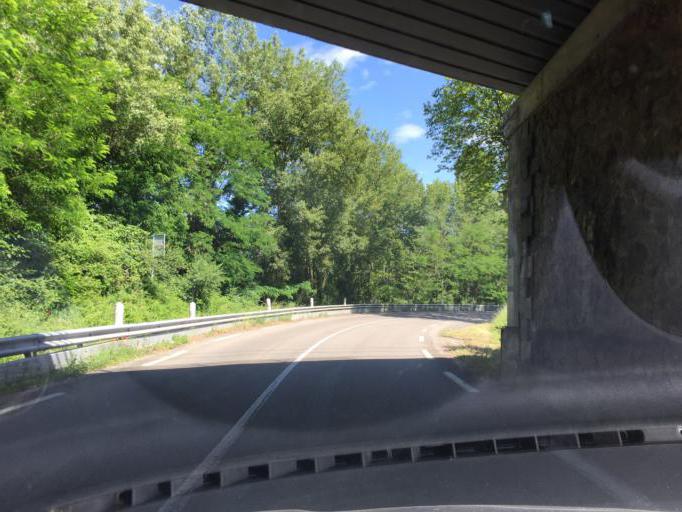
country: FR
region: Rhone-Alpes
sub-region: Departement de l'Ardeche
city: Sarras
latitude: 45.1806
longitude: 4.8009
